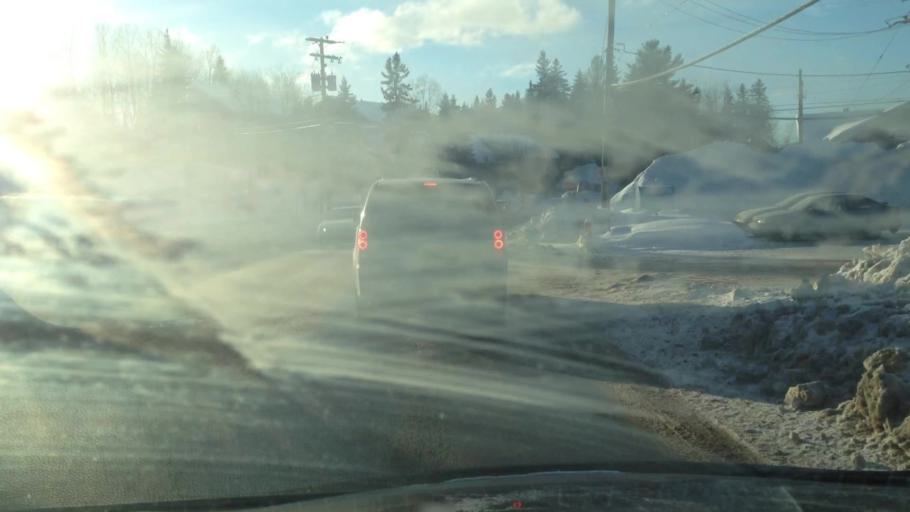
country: CA
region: Quebec
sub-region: Laurentides
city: Saint-Sauveur
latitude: 45.8888
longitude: -74.1447
